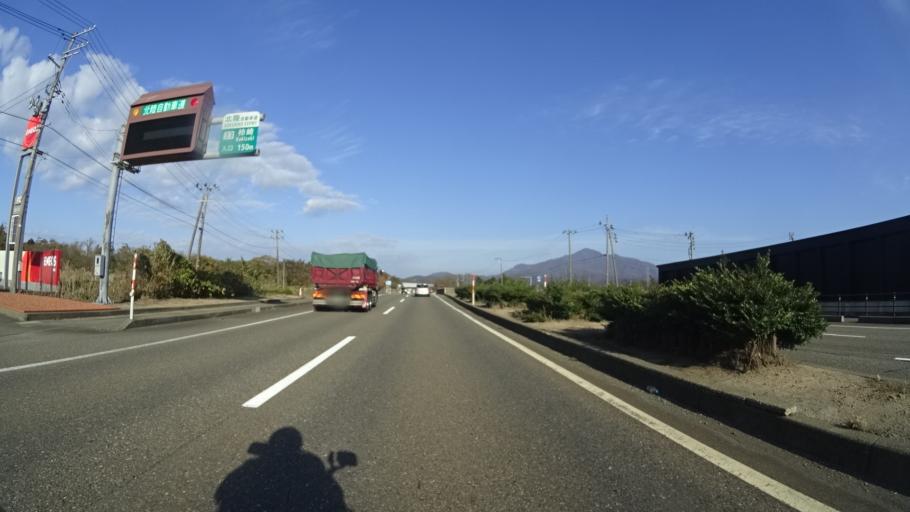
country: JP
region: Niigata
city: Joetsu
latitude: 37.2685
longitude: 138.3840
